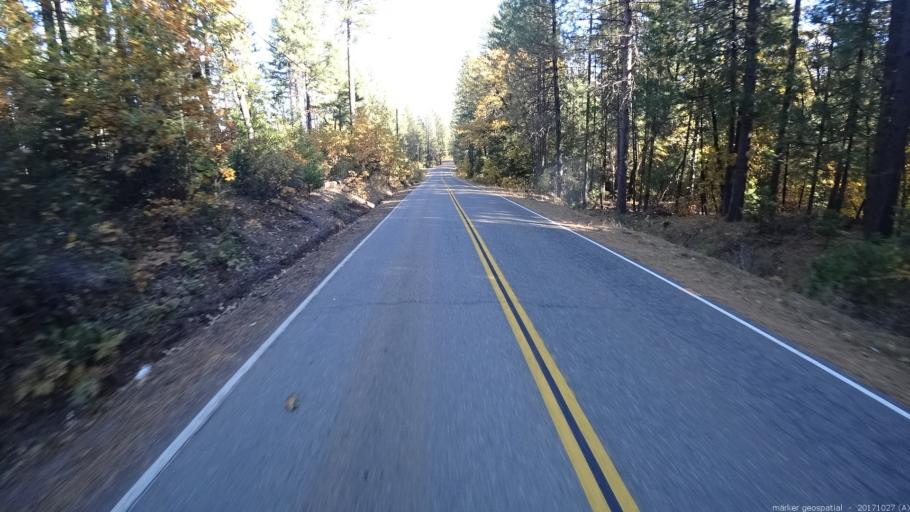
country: US
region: California
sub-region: Shasta County
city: Burney
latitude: 40.9942
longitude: -121.9207
